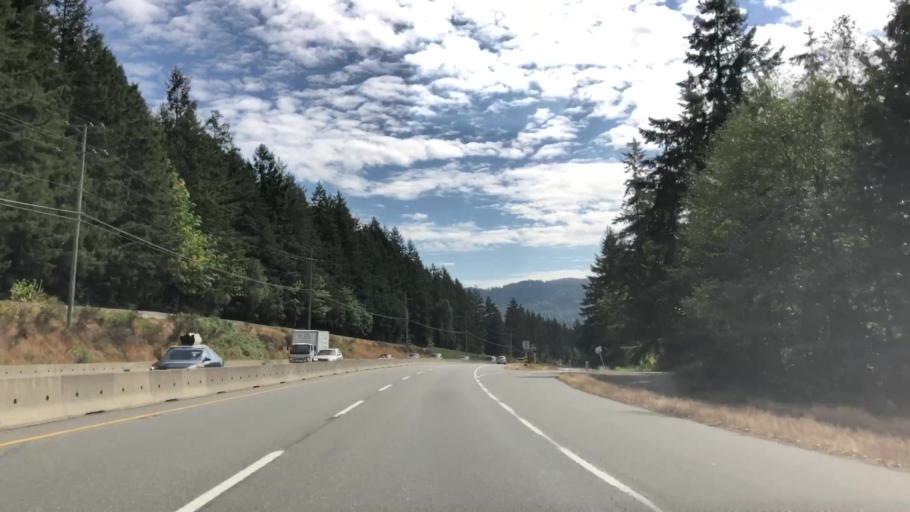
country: CA
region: British Columbia
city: North Cowichan
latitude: 48.8880
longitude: -123.7047
